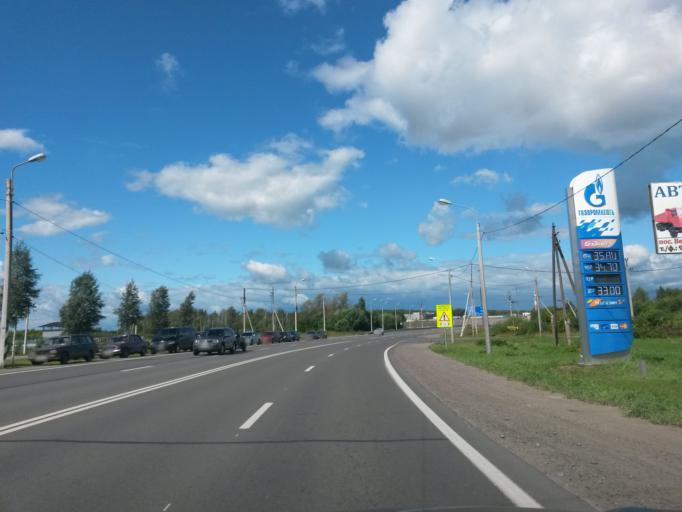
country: RU
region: Jaroslavl
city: Yaroslavl
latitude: 57.6781
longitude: 39.9012
